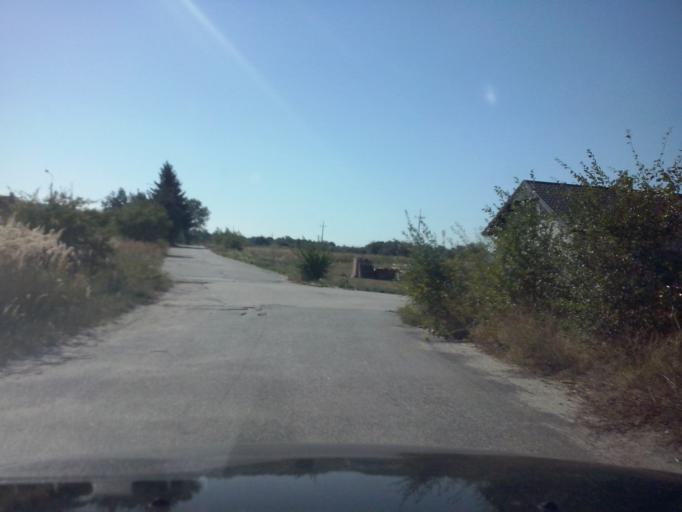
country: PL
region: Swietokrzyskie
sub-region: Powiat kielecki
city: Chmielnik
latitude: 50.6088
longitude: 20.7344
